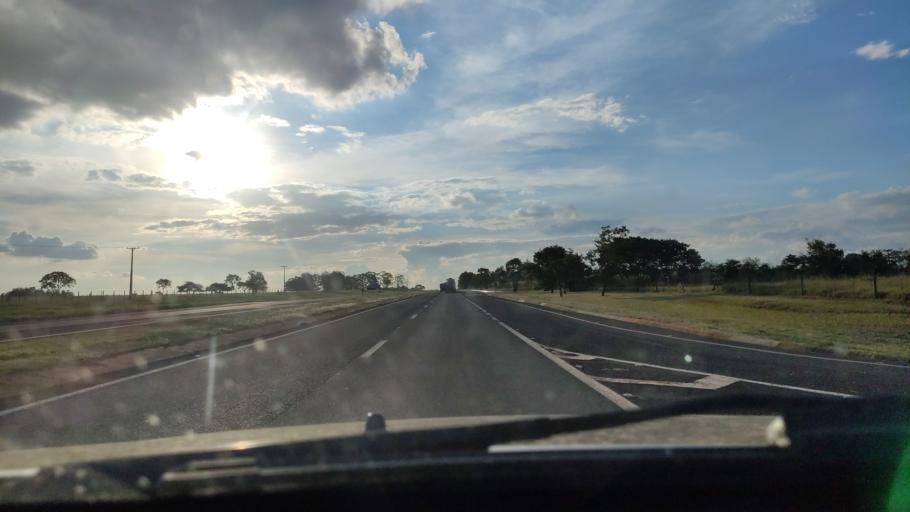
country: BR
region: Sao Paulo
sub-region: Rancharia
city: Rancharia
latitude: -22.4611
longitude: -50.9638
